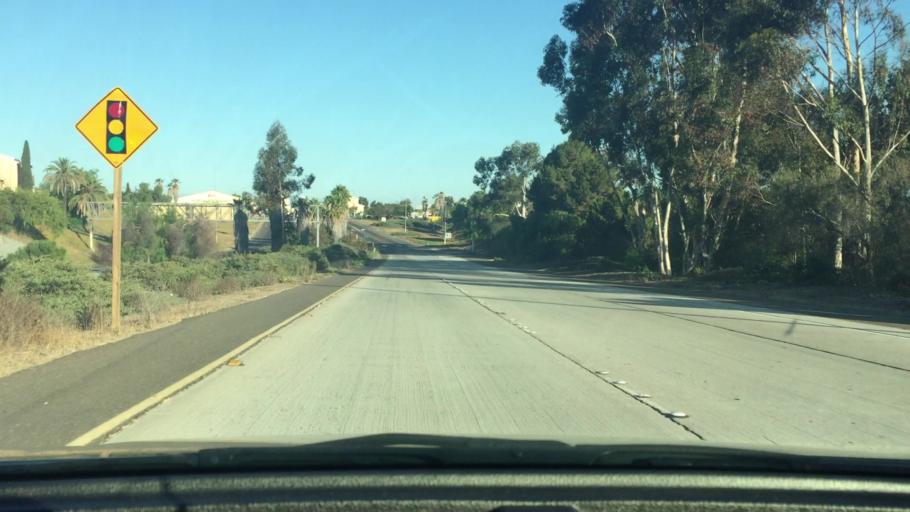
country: US
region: California
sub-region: San Diego County
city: National City
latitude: 32.6909
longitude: -117.0988
